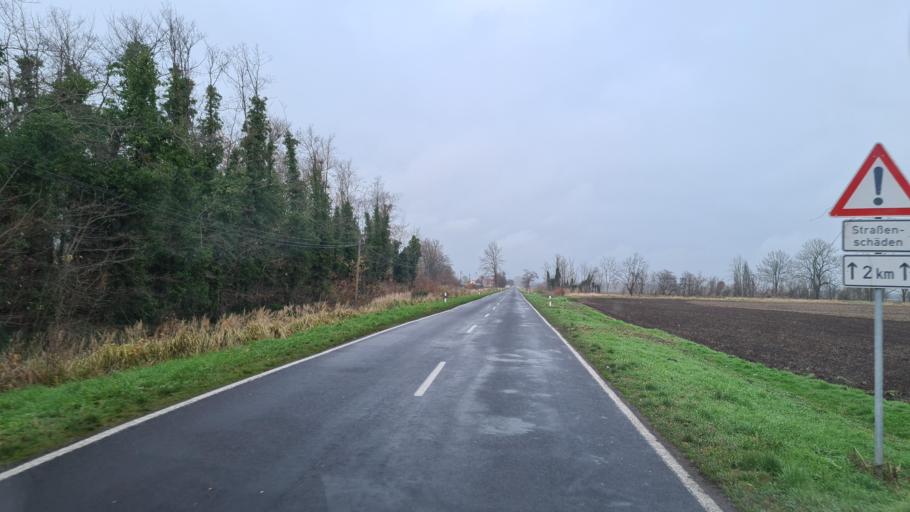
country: DE
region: Brandenburg
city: Nauen
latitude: 52.6258
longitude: 12.7935
